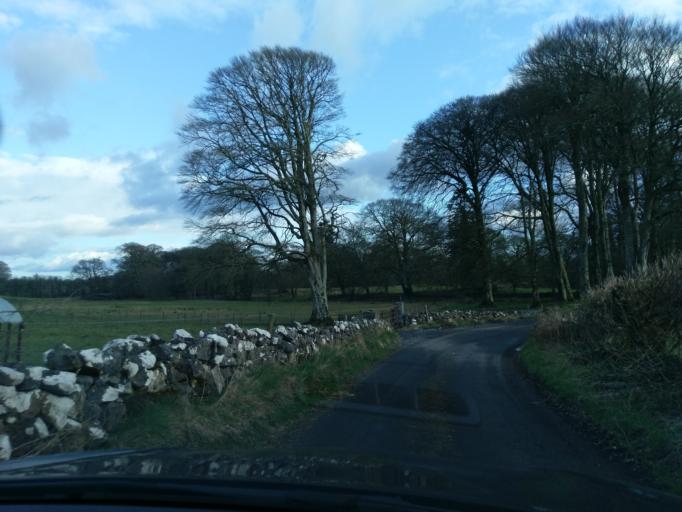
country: IE
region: Connaught
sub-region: County Galway
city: Athenry
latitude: 53.3676
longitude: -8.6504
